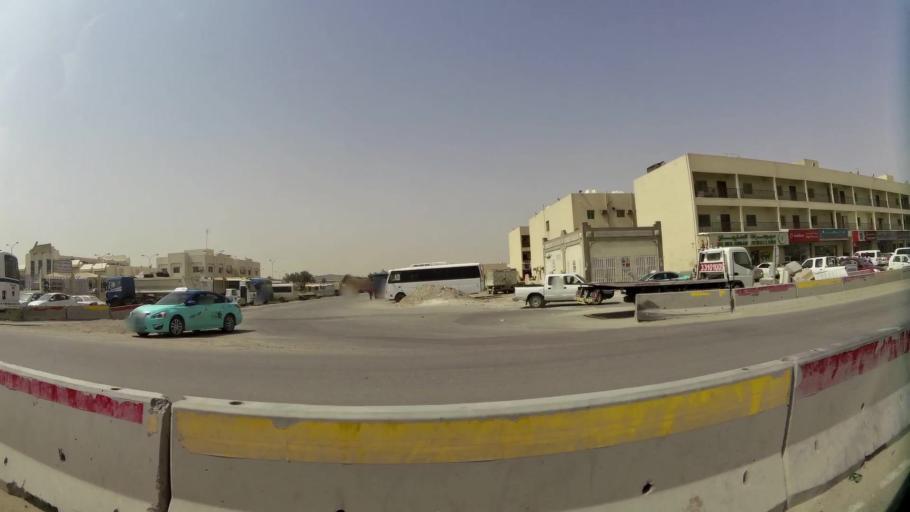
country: QA
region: Baladiyat ar Rayyan
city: Ar Rayyan
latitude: 25.1930
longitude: 51.4332
